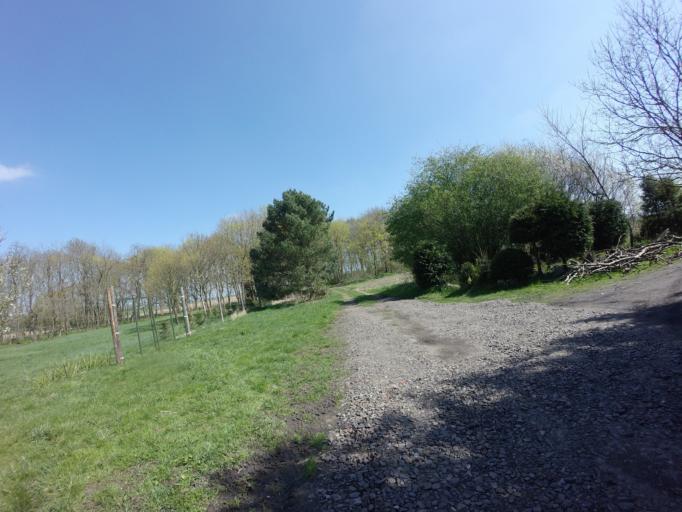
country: PL
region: West Pomeranian Voivodeship
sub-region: Powiat choszczenski
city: Choszczno
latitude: 53.1611
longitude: 15.4672
